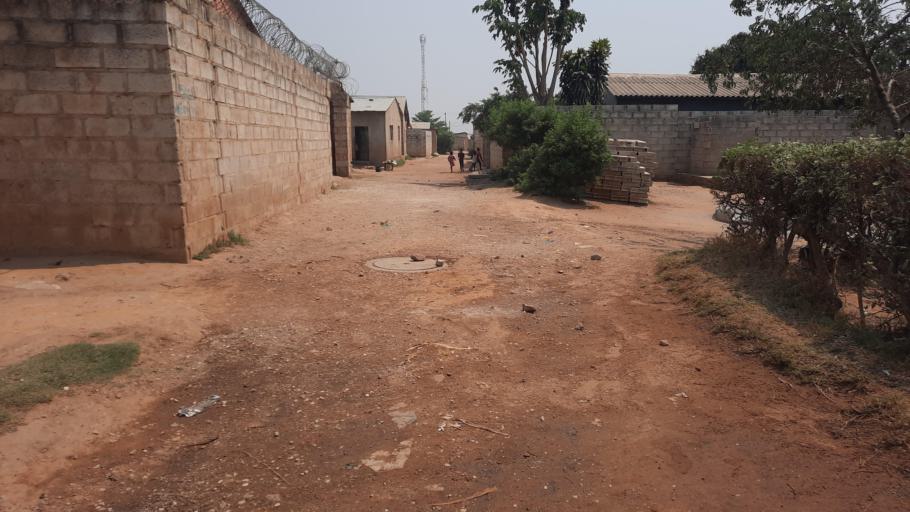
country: ZM
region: Lusaka
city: Lusaka
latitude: -15.3981
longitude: 28.3793
